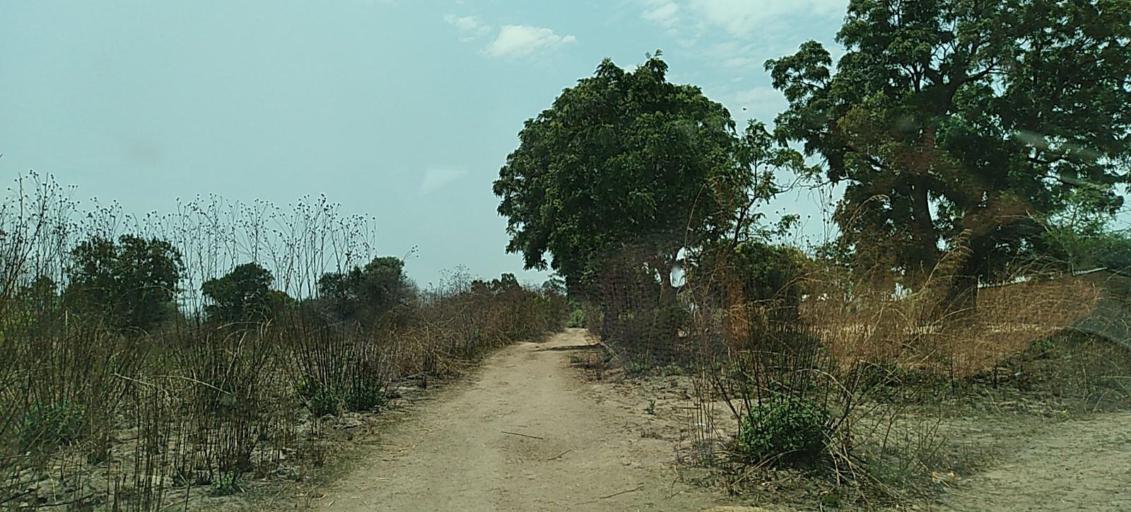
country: ZM
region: Copperbelt
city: Kalulushi
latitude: -12.9529
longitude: 28.1393
